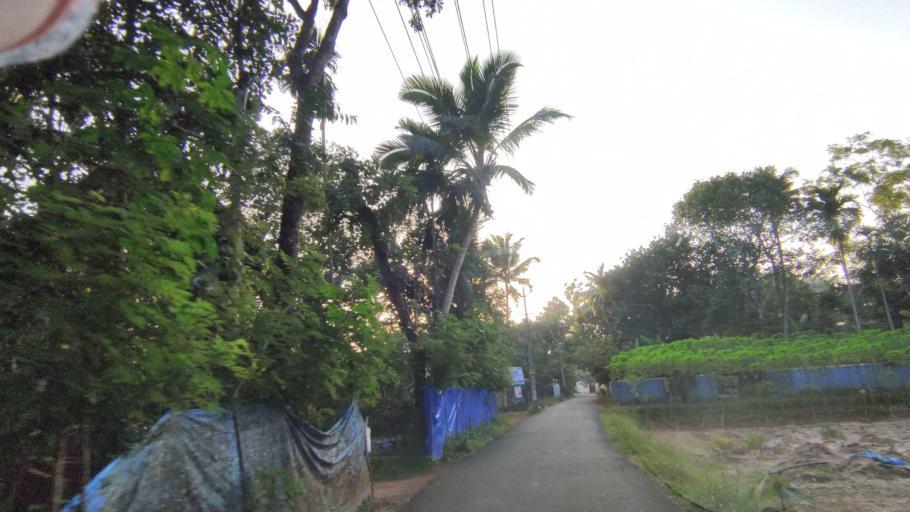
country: IN
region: Kerala
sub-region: Alappuzha
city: Shertallai
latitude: 9.6478
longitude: 76.3428
